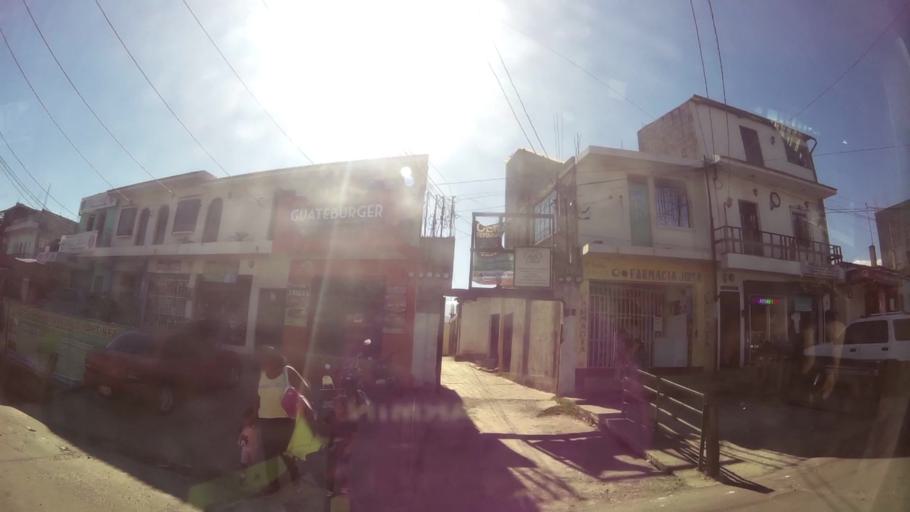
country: GT
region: Guatemala
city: Villa Nueva
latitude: 14.5444
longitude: -90.6167
